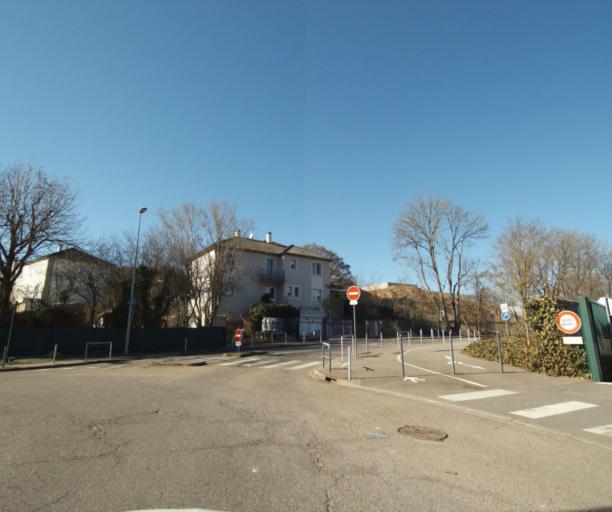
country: FR
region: Lorraine
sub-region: Departement de Meurthe-et-Moselle
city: Vandoeuvre-les-Nancy
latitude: 48.6511
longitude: 6.1763
